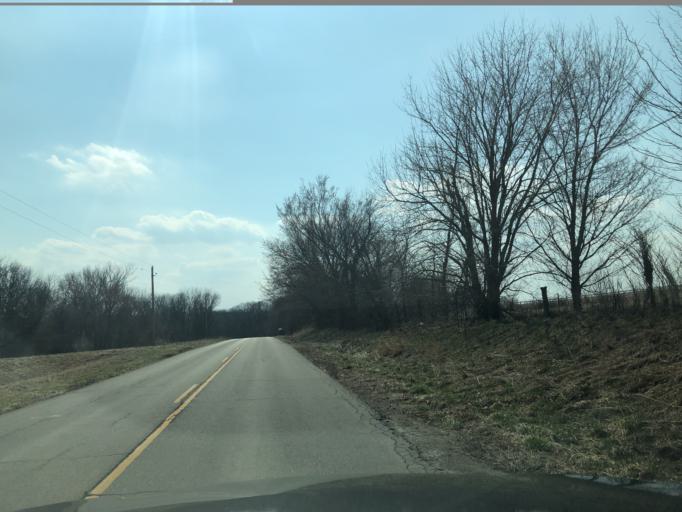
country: US
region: Missouri
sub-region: Platte County
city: Weston
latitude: 39.4256
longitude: -94.8715
